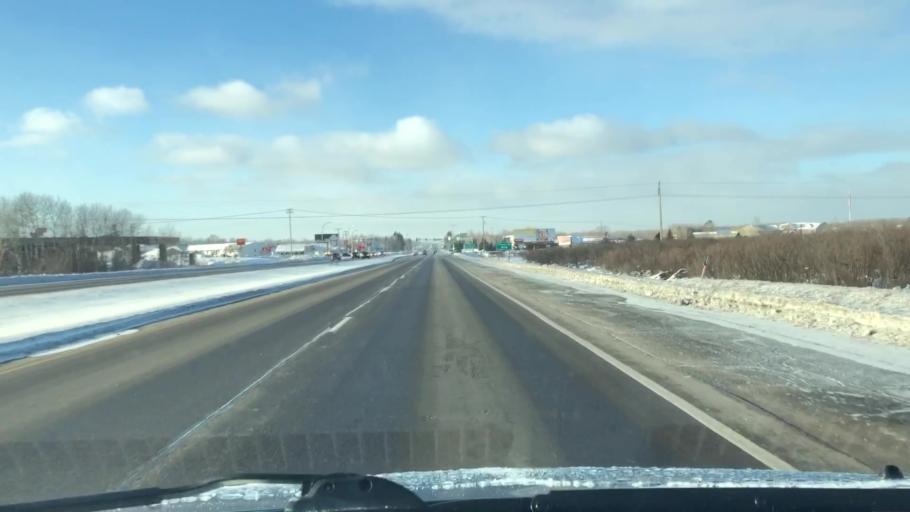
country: US
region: Minnesota
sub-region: Saint Louis County
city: Hermantown
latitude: 46.8129
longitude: -92.1715
